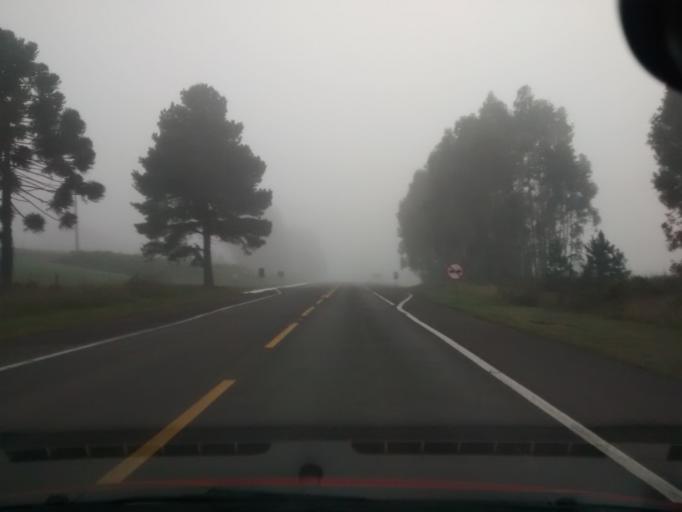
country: BR
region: Rio Grande do Sul
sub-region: Vacaria
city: Vacaria
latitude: -28.2859
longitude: -50.8027
